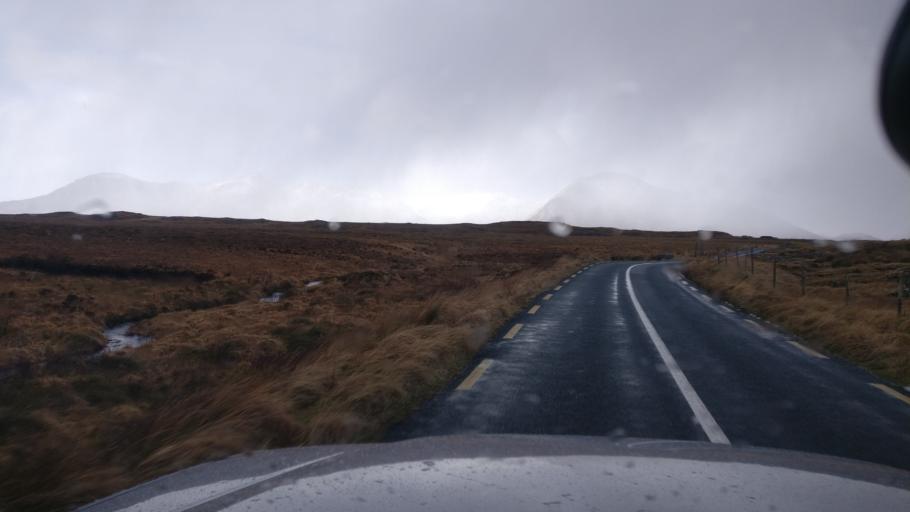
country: IE
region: Connaught
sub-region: County Galway
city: Clifden
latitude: 53.4406
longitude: -9.7710
